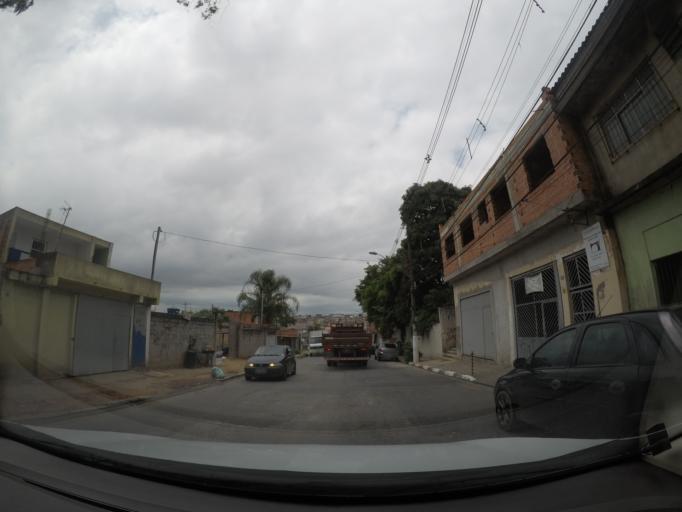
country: BR
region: Sao Paulo
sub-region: Itaquaquecetuba
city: Itaquaquecetuba
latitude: -23.4516
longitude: -46.4037
